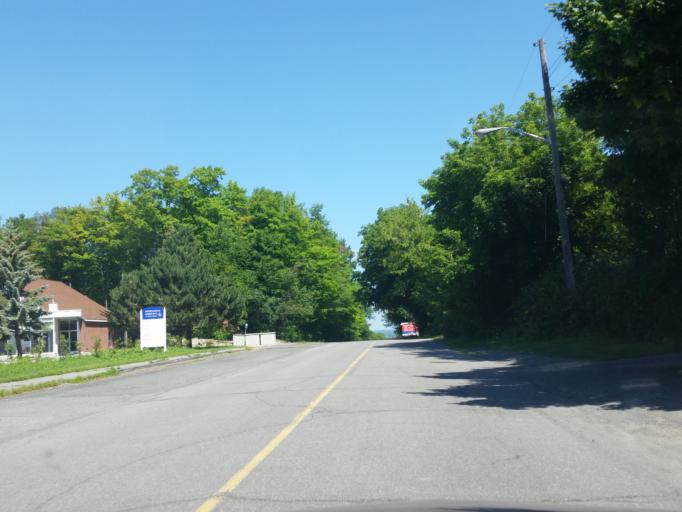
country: CA
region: Ontario
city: Ottawa
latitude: 45.4474
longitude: -75.6317
